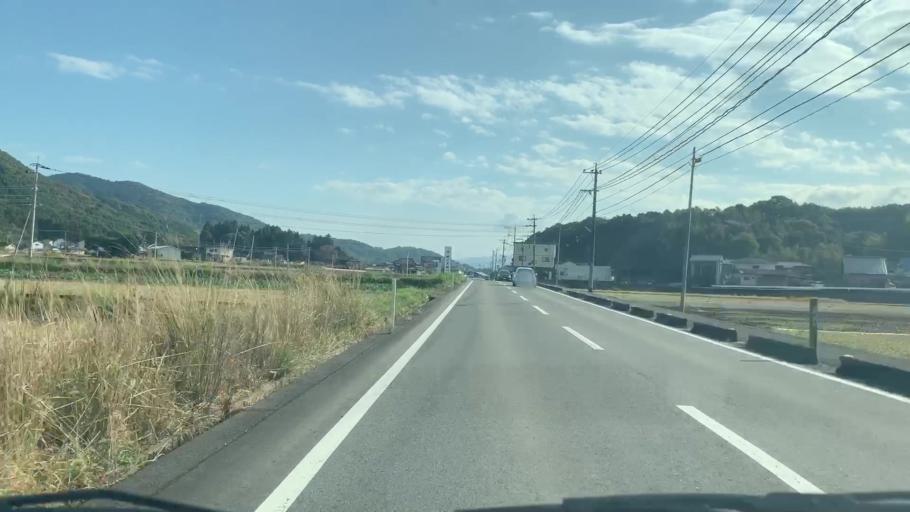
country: JP
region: Saga Prefecture
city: Takeocho-takeo
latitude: 33.1551
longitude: 130.0636
